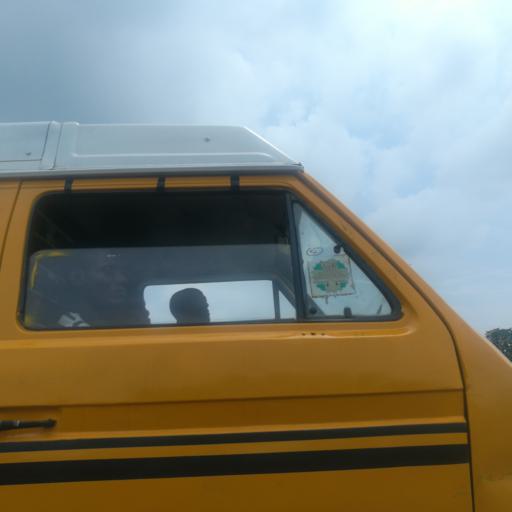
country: NG
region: Lagos
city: Ojota
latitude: 6.5827
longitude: 3.3917
